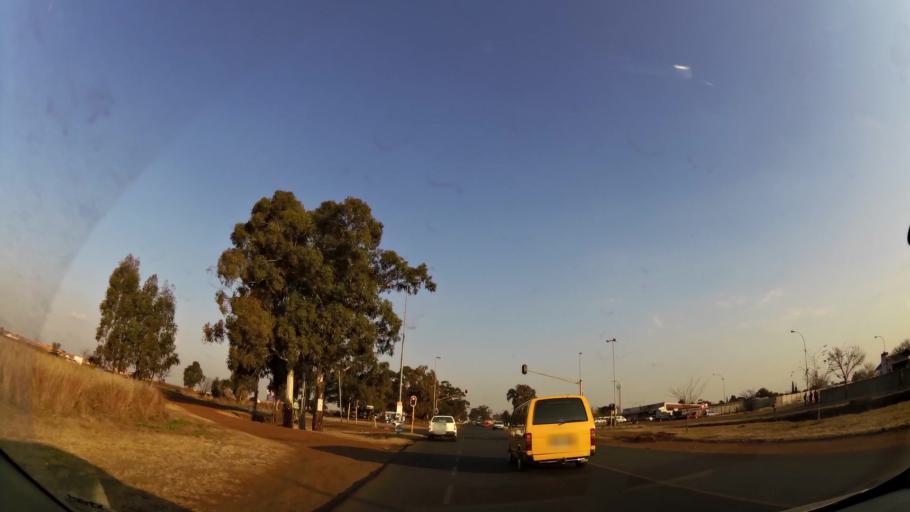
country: ZA
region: Gauteng
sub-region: Ekurhuleni Metropolitan Municipality
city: Germiston
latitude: -26.3076
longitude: 28.2330
